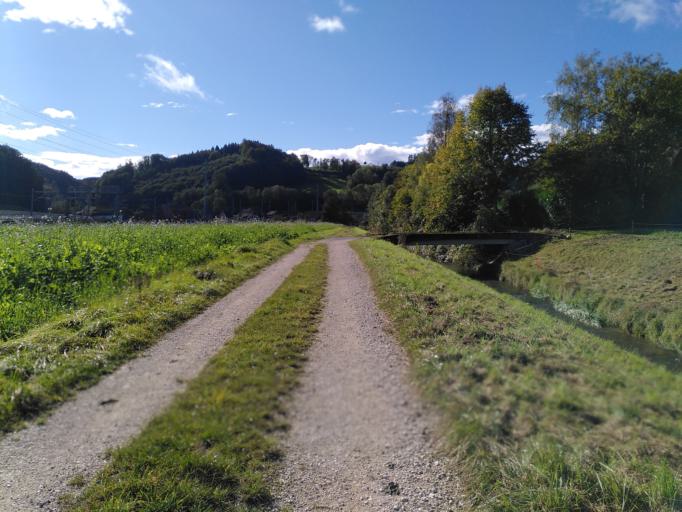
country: CH
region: Bern
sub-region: Oberaargau
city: Seeberg
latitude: 47.1463
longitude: 7.6957
